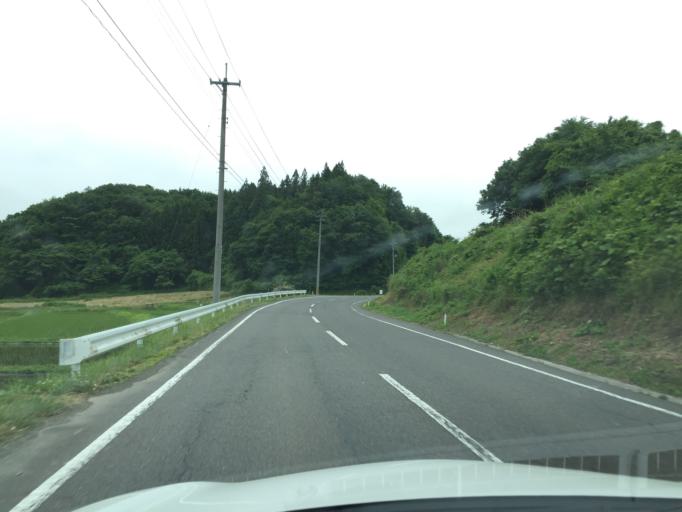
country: JP
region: Fukushima
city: Funehikimachi-funehiki
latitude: 37.3167
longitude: 140.6290
